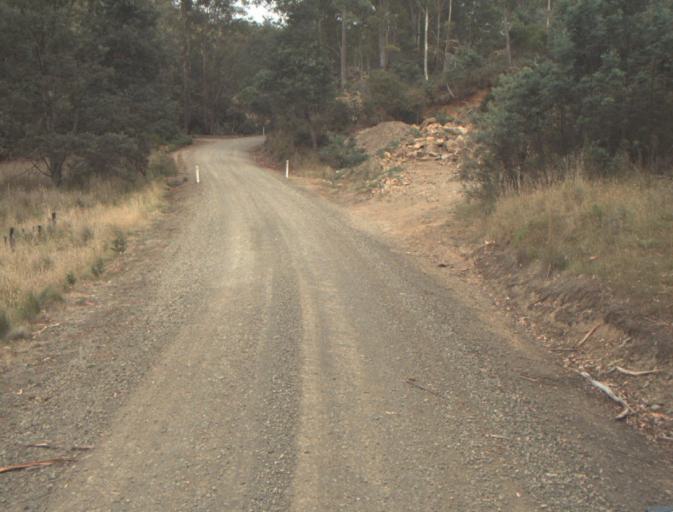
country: AU
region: Tasmania
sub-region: Northern Midlands
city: Evandale
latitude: -41.4585
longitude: 147.4929
